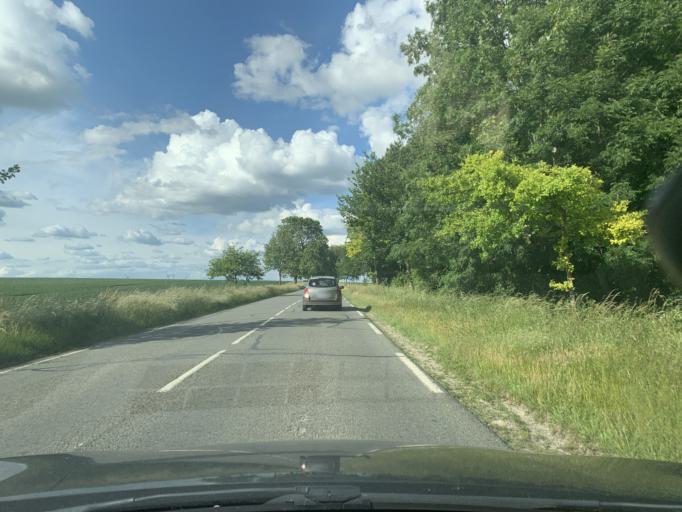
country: FR
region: Picardie
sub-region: Departement de la Somme
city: Moislains
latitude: 49.9736
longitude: 2.9922
